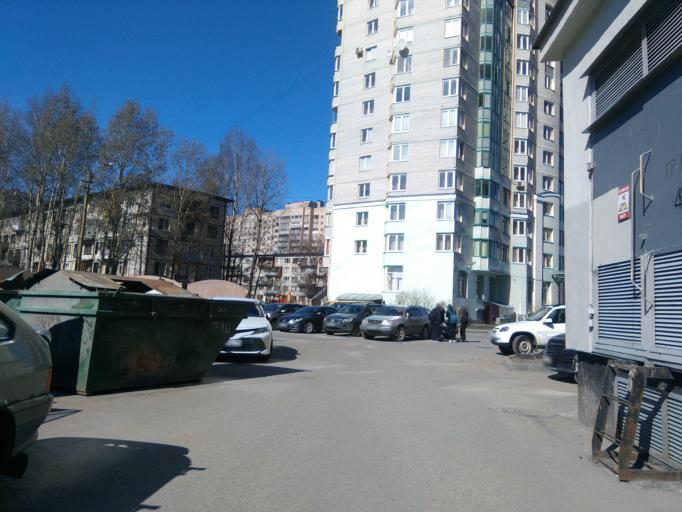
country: RU
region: St.-Petersburg
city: Grazhdanka
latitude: 60.0338
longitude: 30.4169
